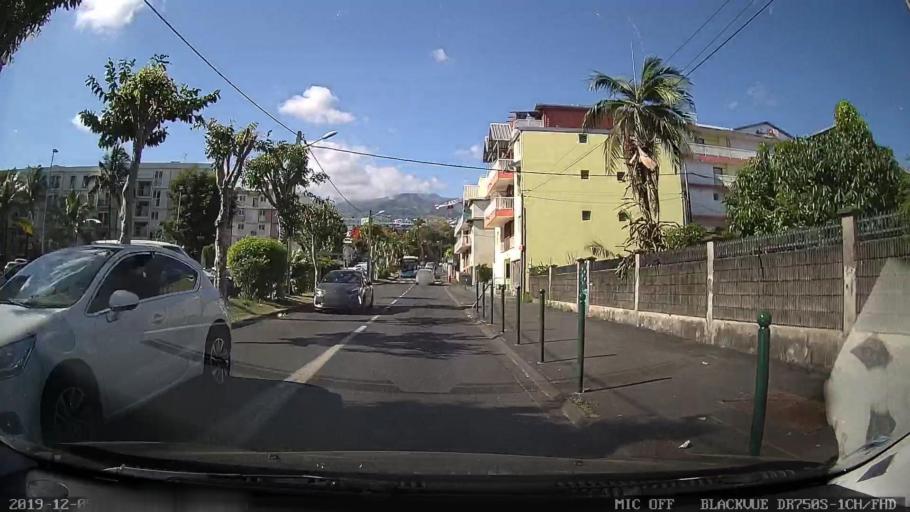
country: RE
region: Reunion
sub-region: Reunion
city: Saint-Denis
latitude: -20.8971
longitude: 55.4807
